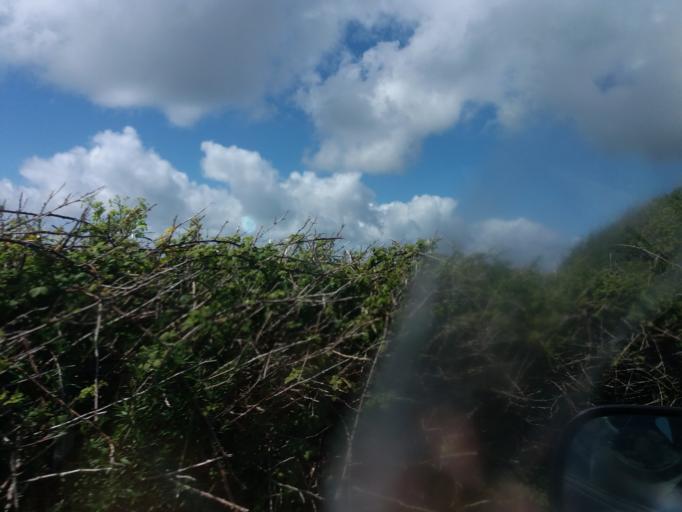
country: IE
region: Munster
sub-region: Waterford
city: Dunmore East
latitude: 52.1808
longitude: -6.8949
